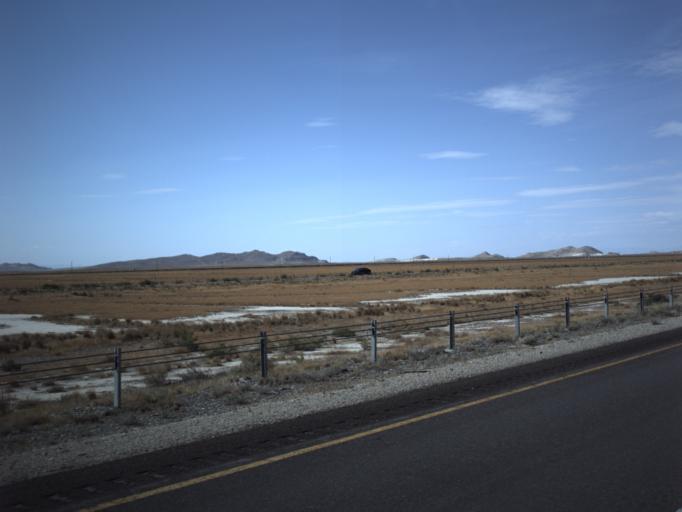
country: US
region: Utah
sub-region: Tooele County
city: Grantsville
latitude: 40.7269
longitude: -113.2151
